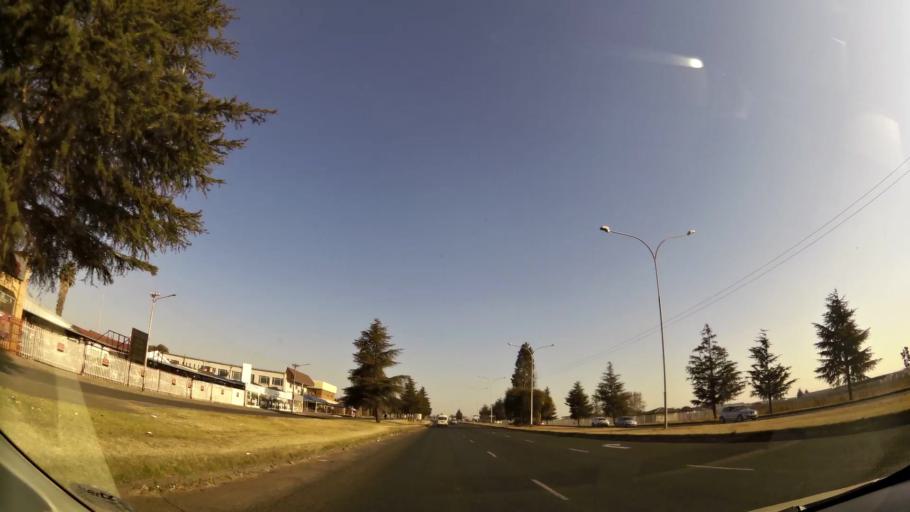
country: ZA
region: Gauteng
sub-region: West Rand District Municipality
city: Randfontein
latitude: -26.1969
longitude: 27.6995
